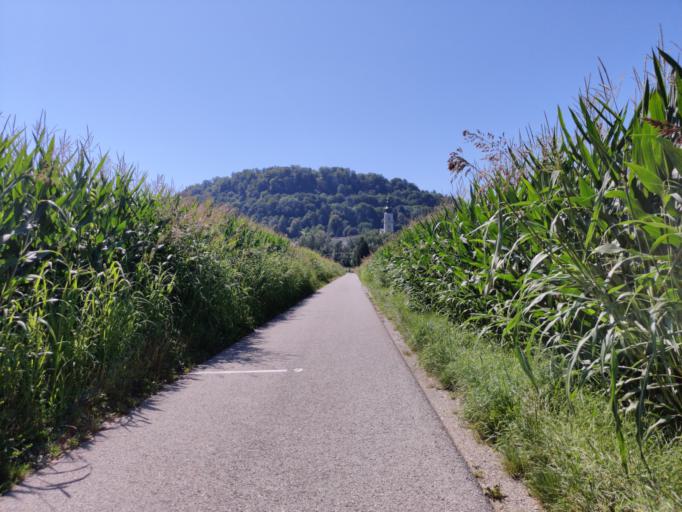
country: AT
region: Styria
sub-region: Politischer Bezirk Leibnitz
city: Wildon
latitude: 46.8918
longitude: 15.5067
